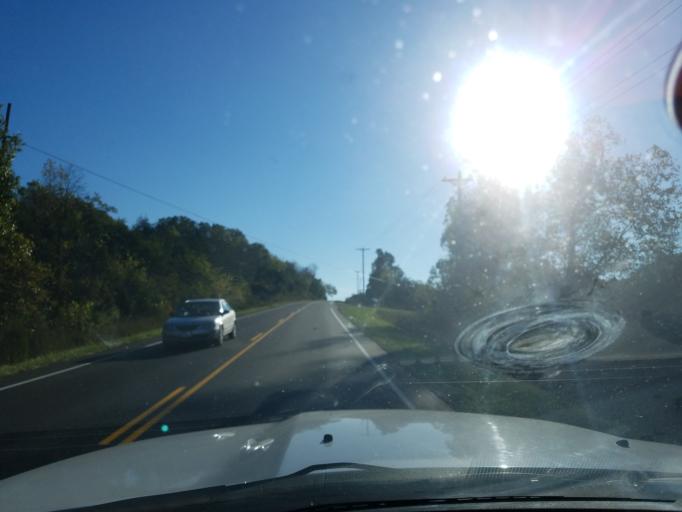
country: US
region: Kentucky
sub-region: Nelson County
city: Bardstown
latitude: 37.7875
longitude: -85.4106
